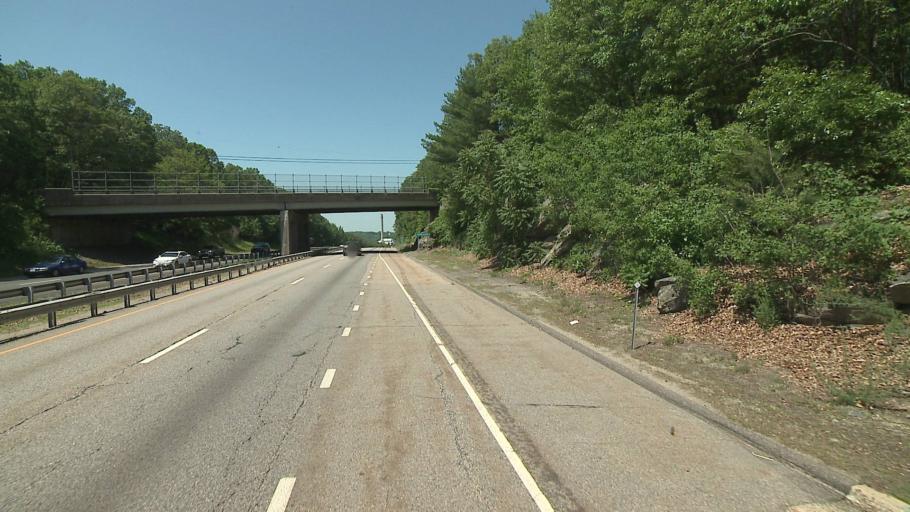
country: US
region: Connecticut
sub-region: New London County
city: Lisbon
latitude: 41.5873
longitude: -72.0297
